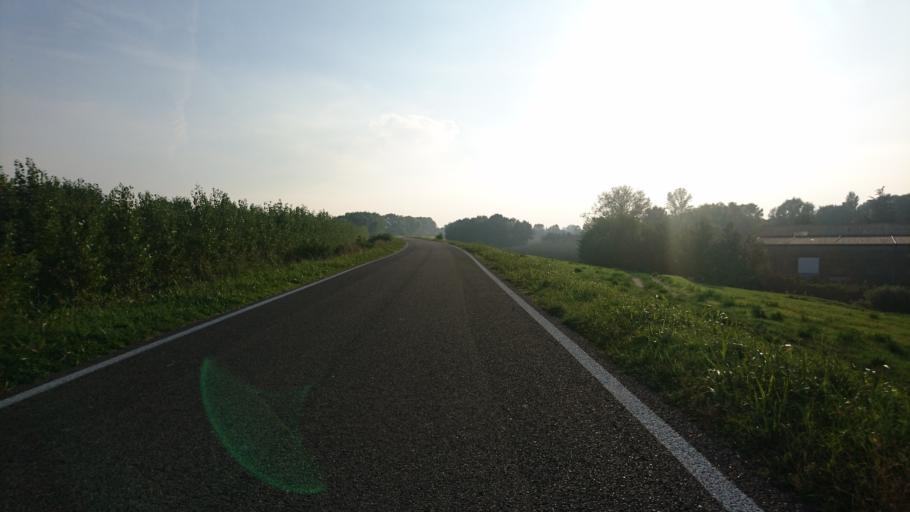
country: IT
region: Emilia-Romagna
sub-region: Provincia di Ferrara
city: Francolino
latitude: 44.9073
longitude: 11.6512
